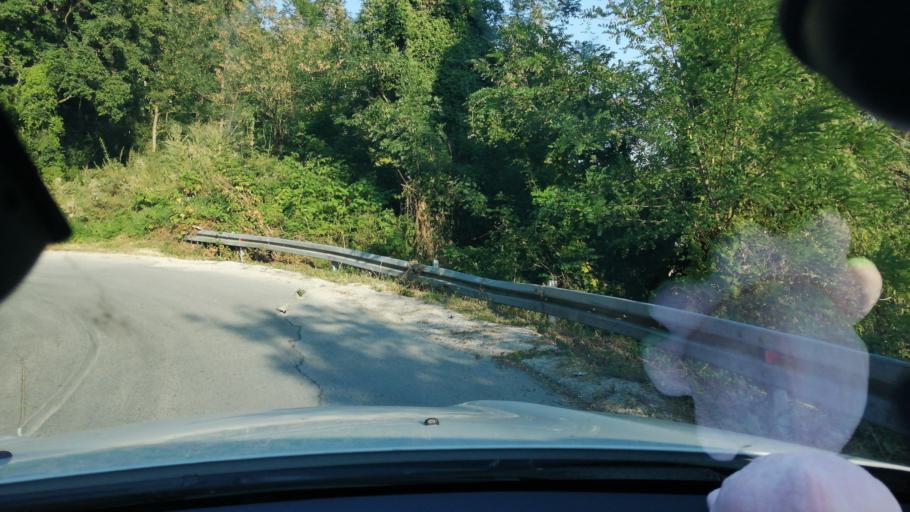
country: RS
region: Central Serbia
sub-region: Moravicki Okrug
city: Cacak
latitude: 43.8390
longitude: 20.2765
